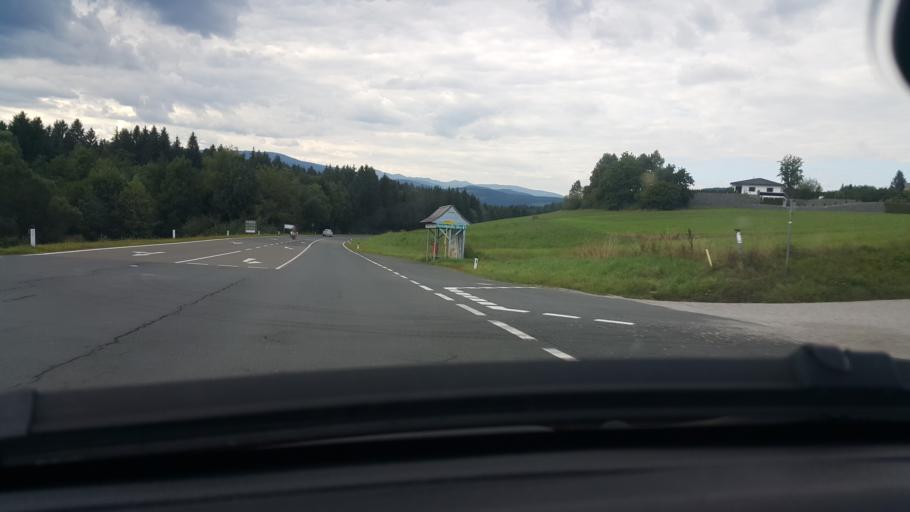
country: AT
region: Carinthia
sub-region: Politischer Bezirk Feldkirchen
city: Feldkirchen in Karnten
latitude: 46.6994
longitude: 14.1211
